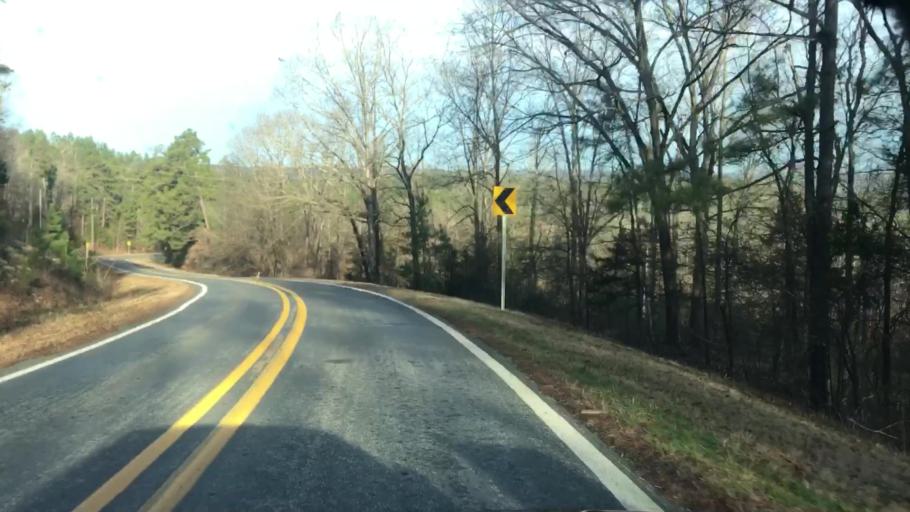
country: US
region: Arkansas
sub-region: Garland County
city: Rockwell
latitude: 34.4877
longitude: -93.2738
